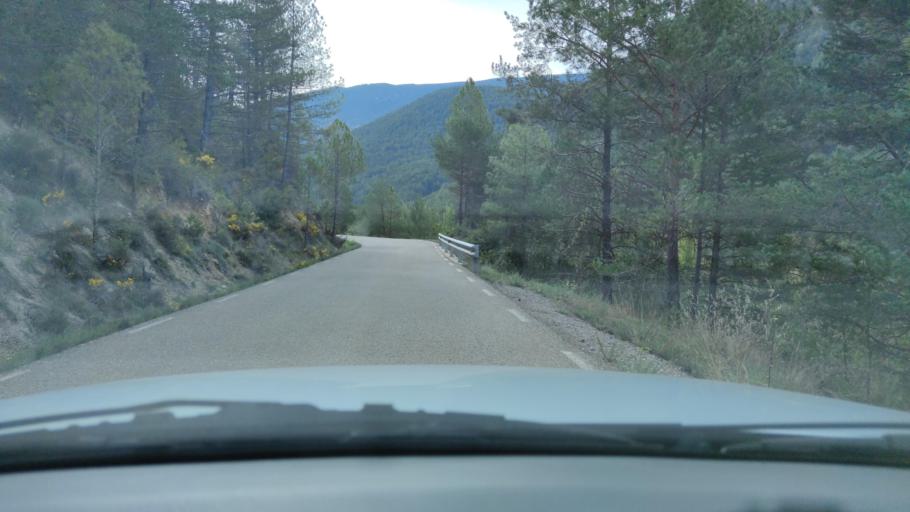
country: ES
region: Catalonia
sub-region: Provincia de Lleida
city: la Seu d'Urgell
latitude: 42.2349
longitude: 1.4662
